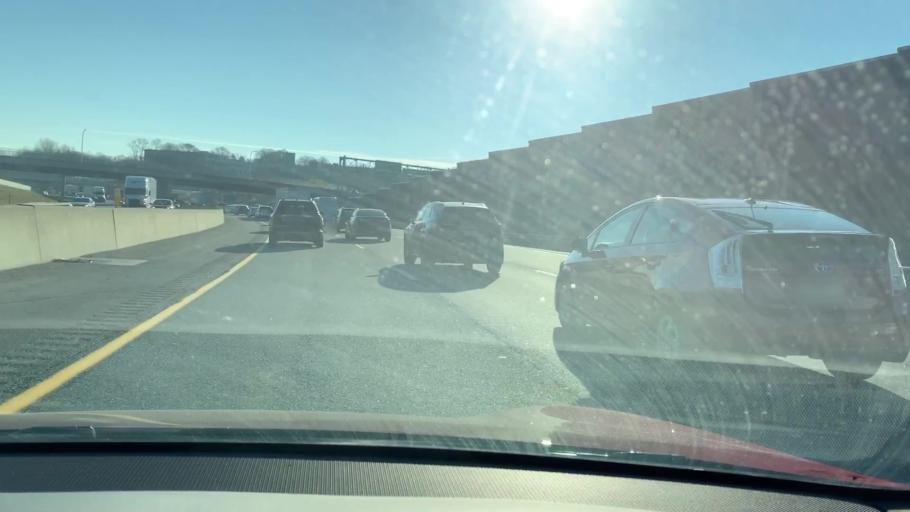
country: US
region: New York
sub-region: Westchester County
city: White Plains
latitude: 41.0319
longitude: -73.7519
